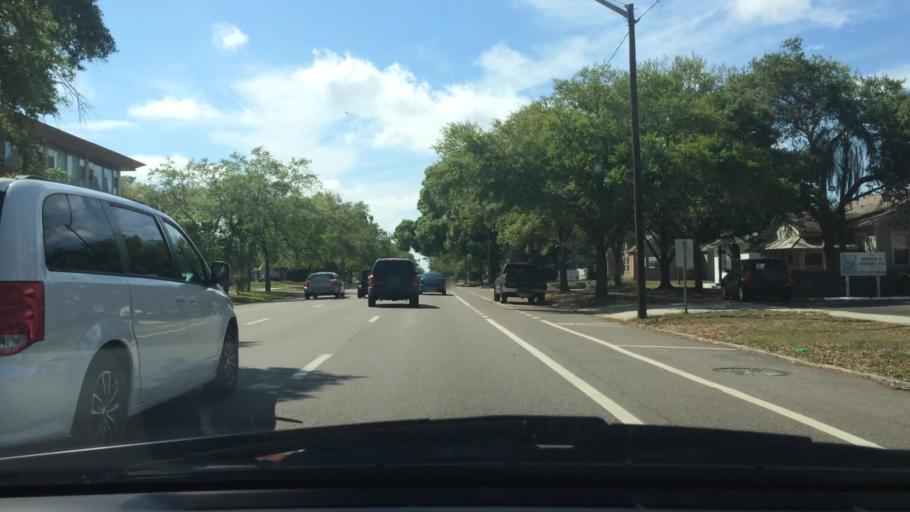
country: US
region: Florida
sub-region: Pinellas County
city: Saint Petersburg
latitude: 27.7719
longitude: -82.6813
